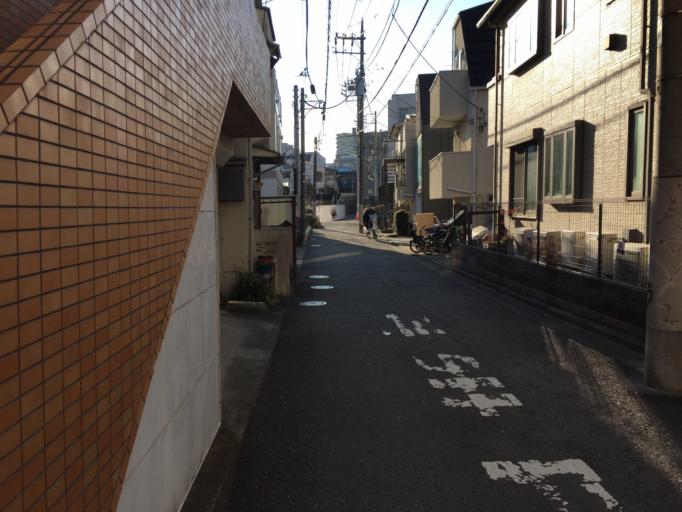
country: JP
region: Tokyo
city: Tokyo
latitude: 35.6517
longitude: 139.6779
